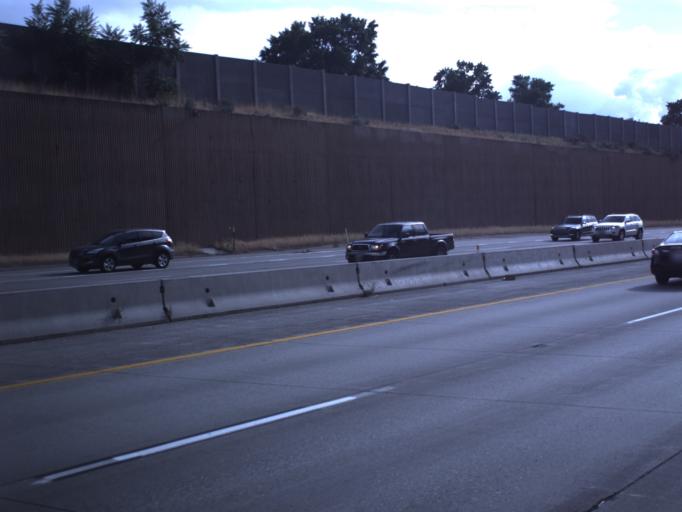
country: US
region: Utah
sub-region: Salt Lake County
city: Little Cottonwood Creek Valley
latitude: 40.6314
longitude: -111.8411
